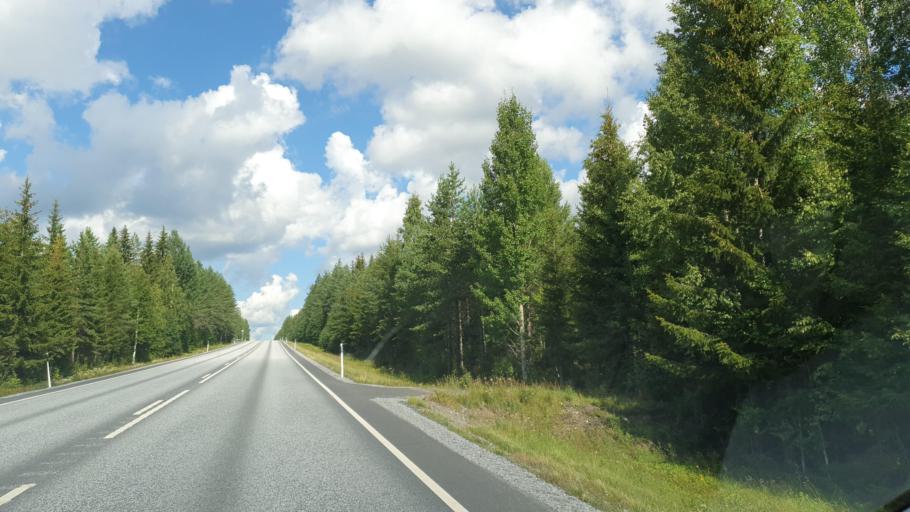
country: FI
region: Northern Savo
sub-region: Ylae-Savo
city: Sonkajaervi
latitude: 63.9161
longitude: 27.3835
